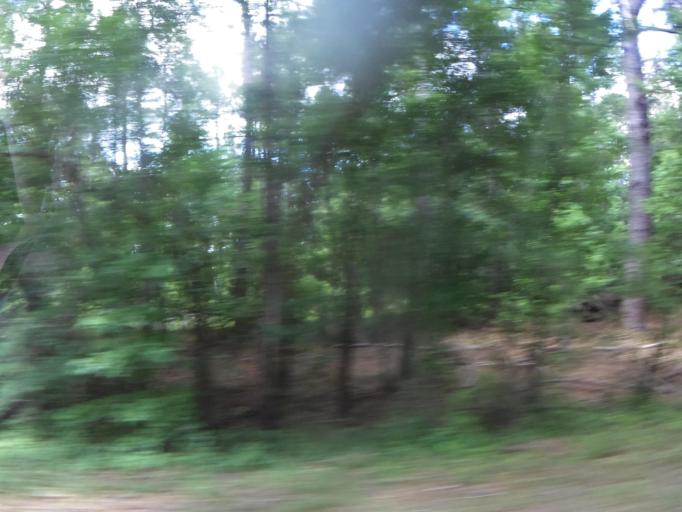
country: US
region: Florida
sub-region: Clay County
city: Asbury Lake
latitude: 29.9113
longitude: -81.8856
